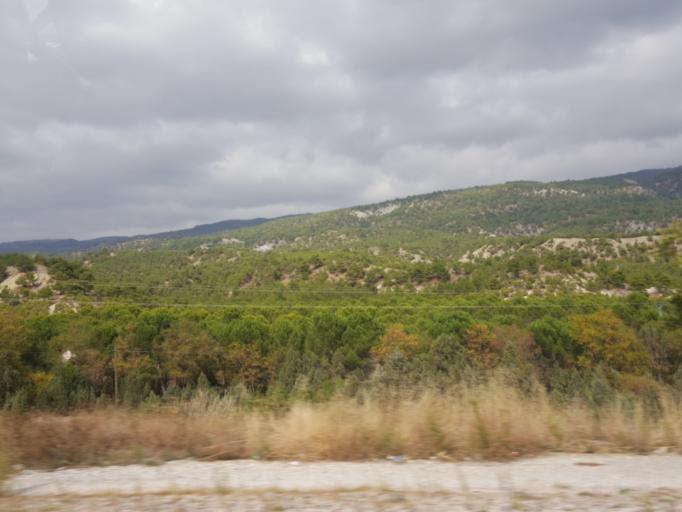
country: TR
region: Corum
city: Hacihamza
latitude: 41.0978
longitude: 34.3575
